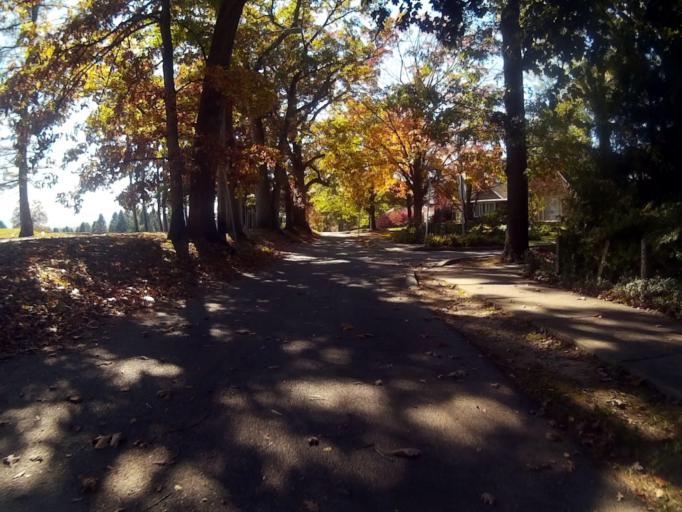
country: US
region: Pennsylvania
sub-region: Centre County
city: State College
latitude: 40.7956
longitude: -77.8735
